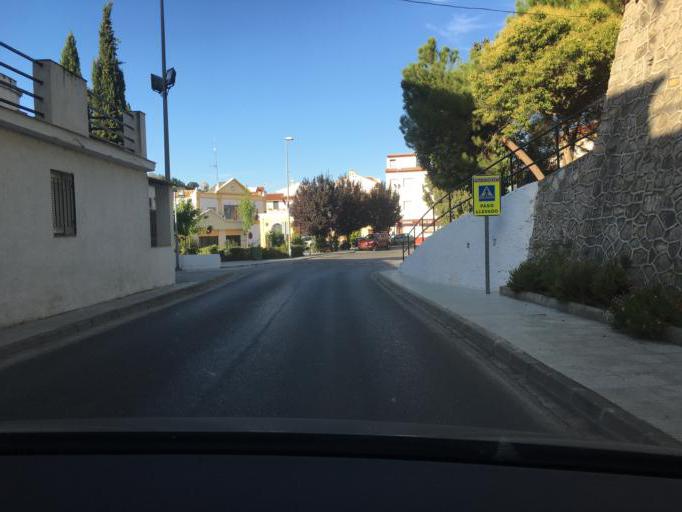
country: ES
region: Andalusia
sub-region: Provincia de Granada
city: Dudar
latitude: 37.1865
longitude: -3.4829
